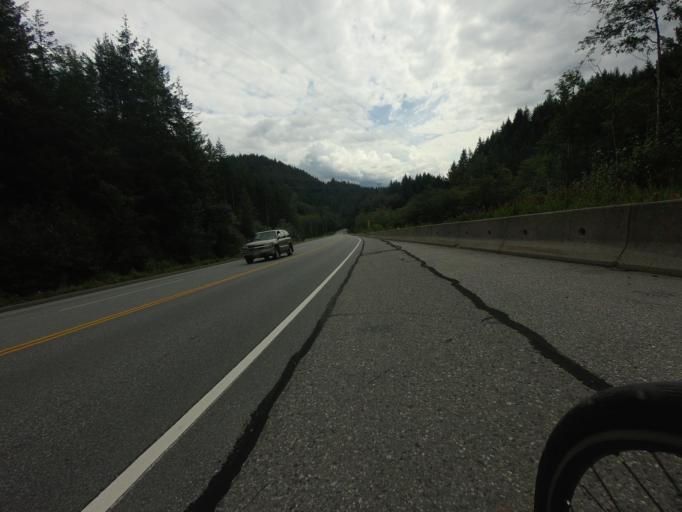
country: CA
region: British Columbia
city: Whistler
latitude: 49.8059
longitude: -123.1228
